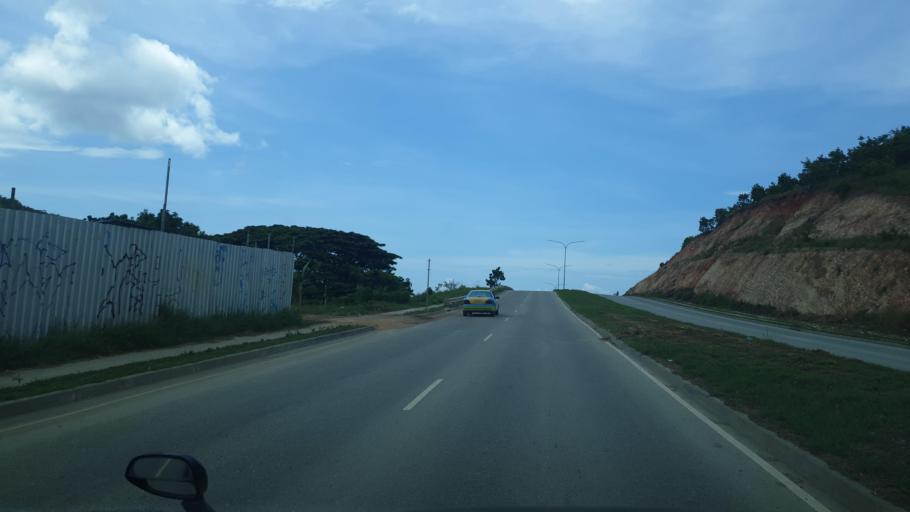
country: PG
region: National Capital
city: Port Moresby
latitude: -9.4336
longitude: 147.1402
